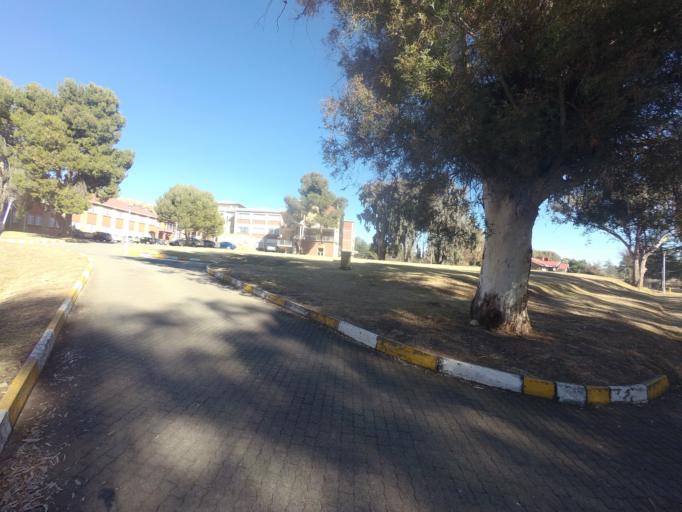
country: LS
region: Maseru
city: Nako
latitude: -29.4484
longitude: 27.7226
